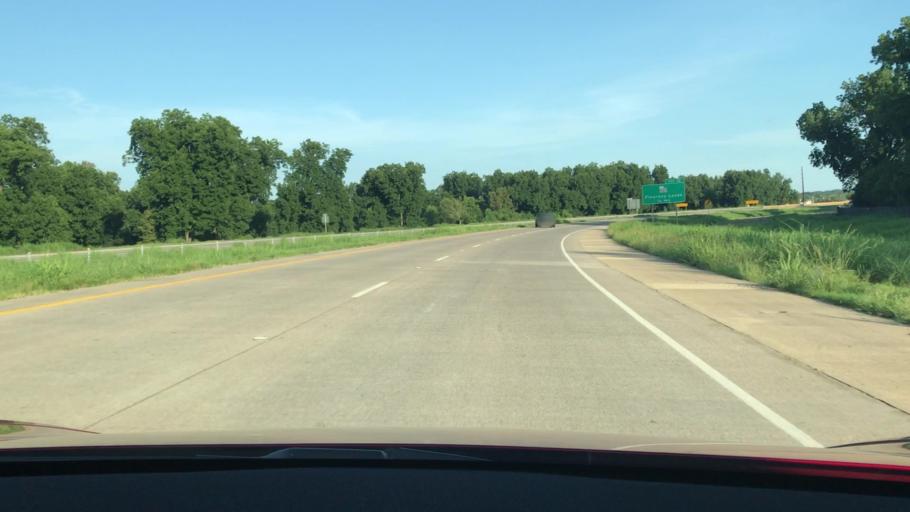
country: US
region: Louisiana
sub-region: Bossier Parish
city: Bossier City
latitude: 32.4081
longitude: -93.7165
